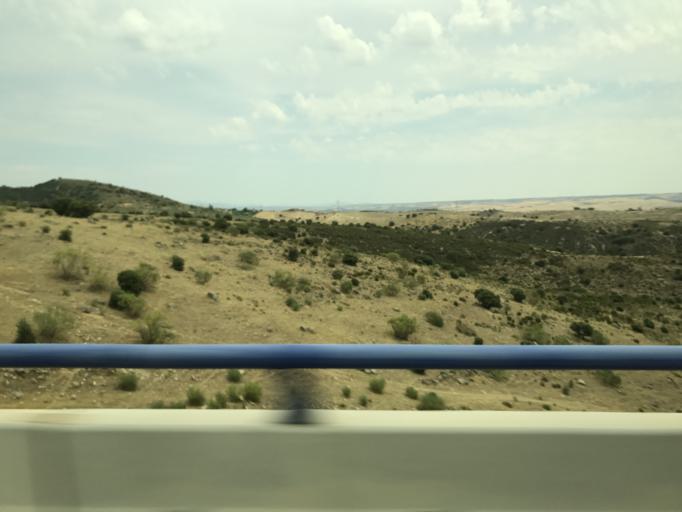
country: ES
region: Madrid
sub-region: Provincia de Madrid
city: El Molar
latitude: 40.7439
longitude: -3.5696
